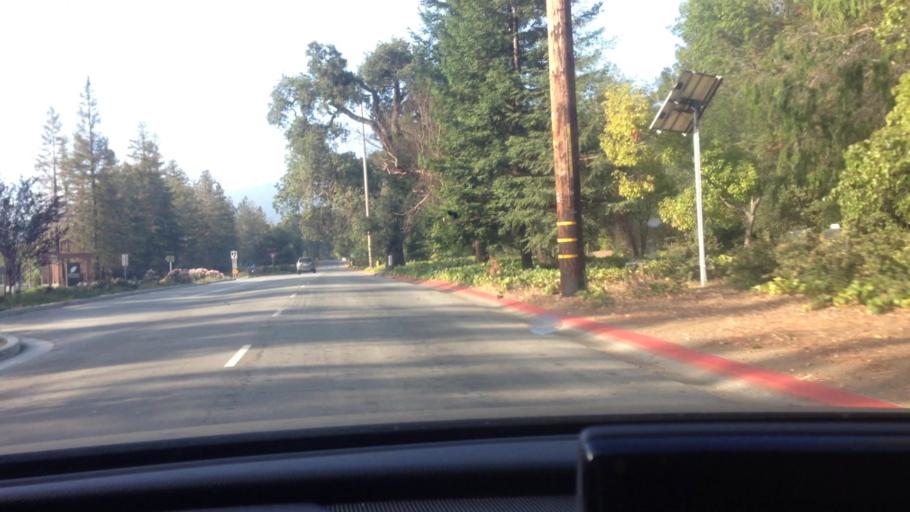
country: US
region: California
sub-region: Santa Clara County
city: Saratoga
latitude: 37.2644
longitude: -122.0140
